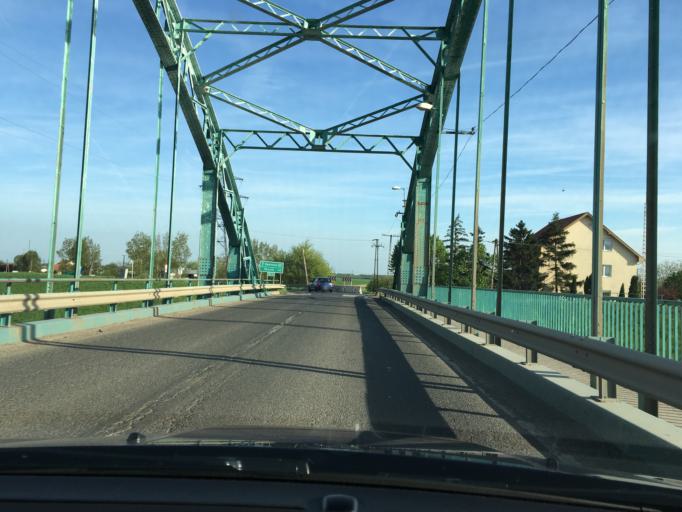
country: HU
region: Bekes
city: Szeghalom
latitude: 47.0135
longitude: 21.1791
